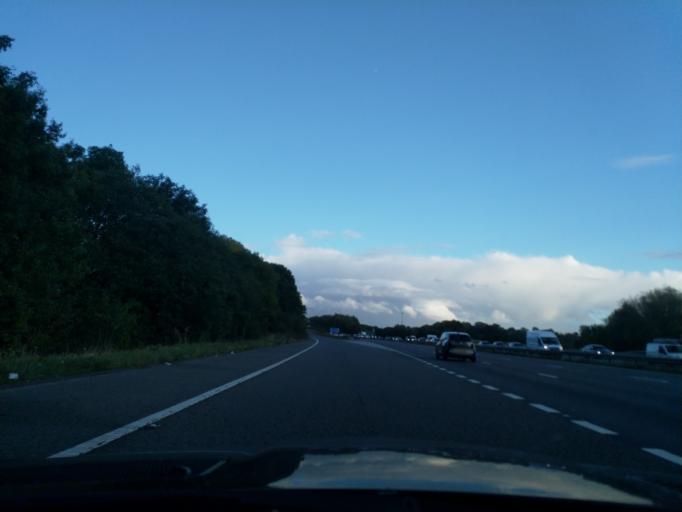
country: GB
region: England
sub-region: Warwickshire
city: Henley in Arden
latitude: 52.3368
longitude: -1.7801
